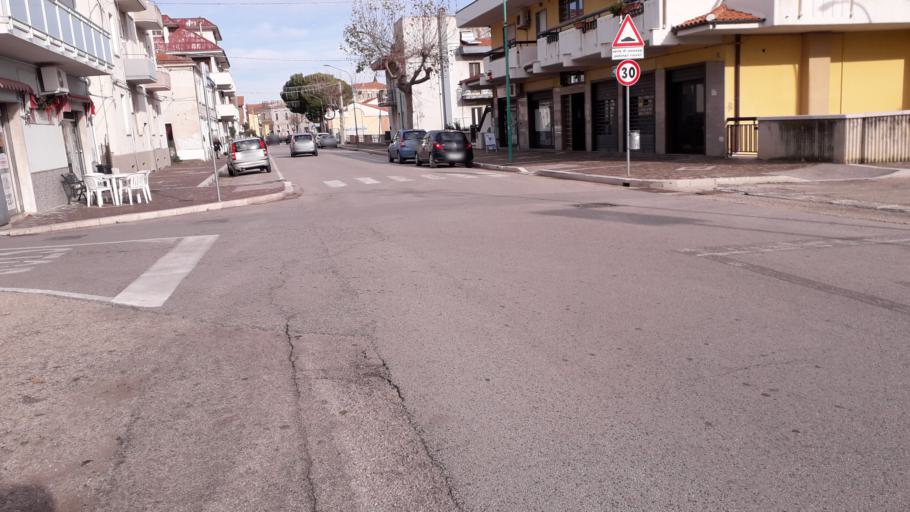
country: IT
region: Molise
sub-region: Provincia di Campobasso
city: Campomarino
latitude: 41.9550
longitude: 15.0356
